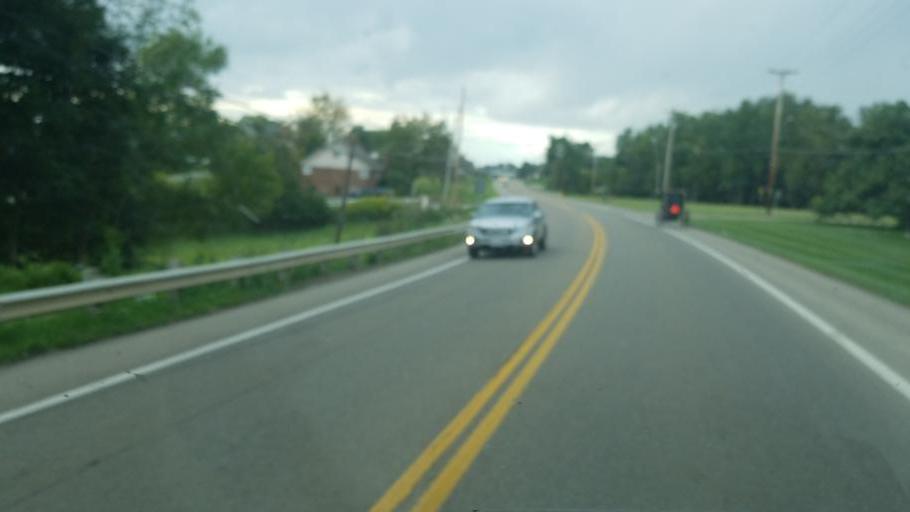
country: US
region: Ohio
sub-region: Tuscarawas County
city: Sugarcreek
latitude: 40.5438
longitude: -81.7305
